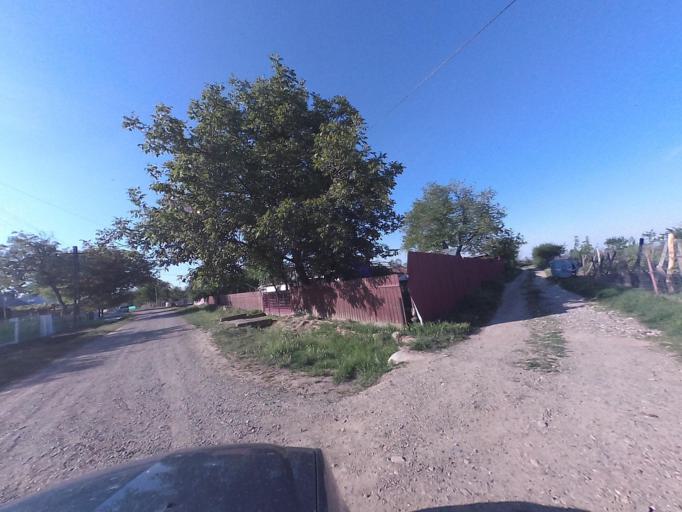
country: RO
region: Neamt
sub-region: Comuna Cordun
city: Pildesti
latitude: 46.9834
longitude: 26.8073
